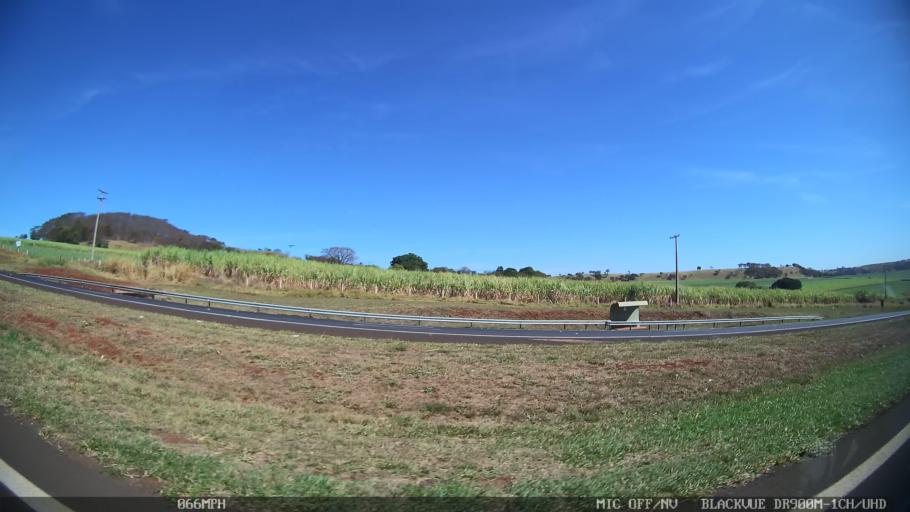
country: BR
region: Sao Paulo
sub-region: Cravinhos
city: Cravinhos
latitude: -21.4236
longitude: -47.6572
